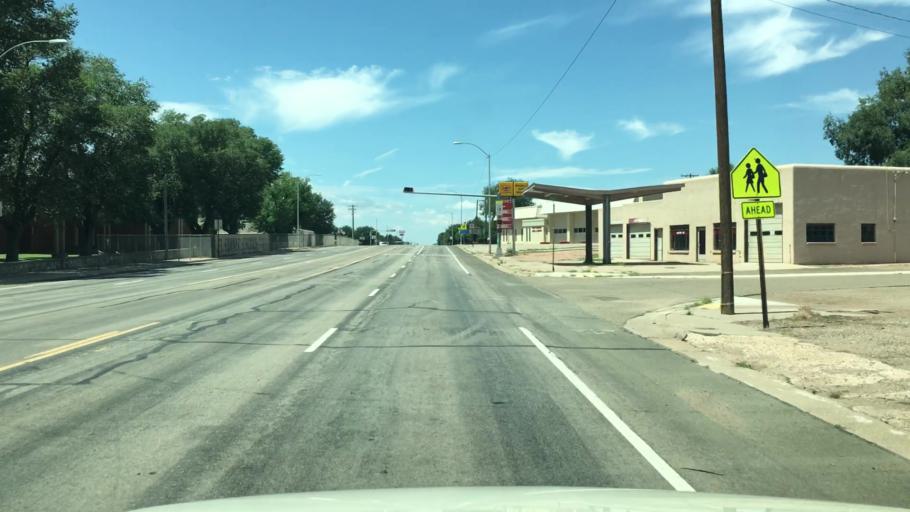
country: US
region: New Mexico
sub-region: De Baca County
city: Fort Sumner
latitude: 34.4689
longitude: -104.2365
